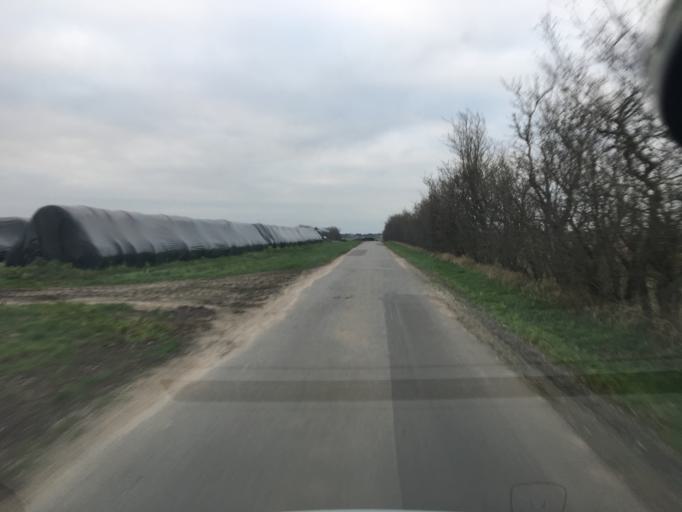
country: DK
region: South Denmark
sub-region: Tonder Kommune
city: Logumkloster
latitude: 55.0496
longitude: 9.0449
